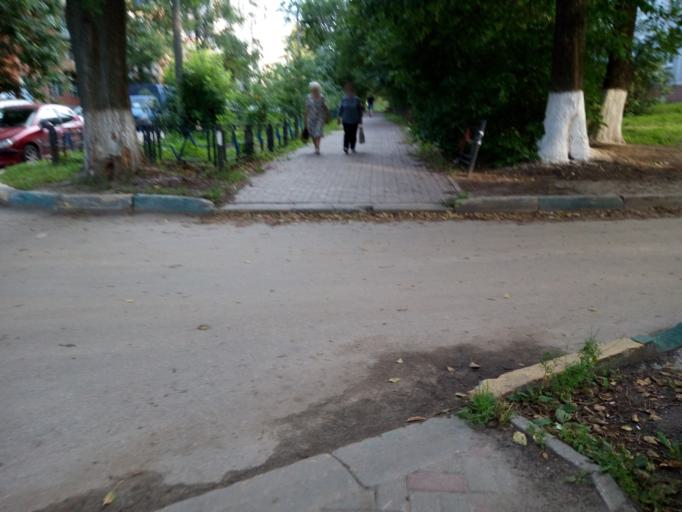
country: RU
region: Nizjnij Novgorod
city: Nizhniy Novgorod
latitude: 56.2706
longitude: 43.9828
